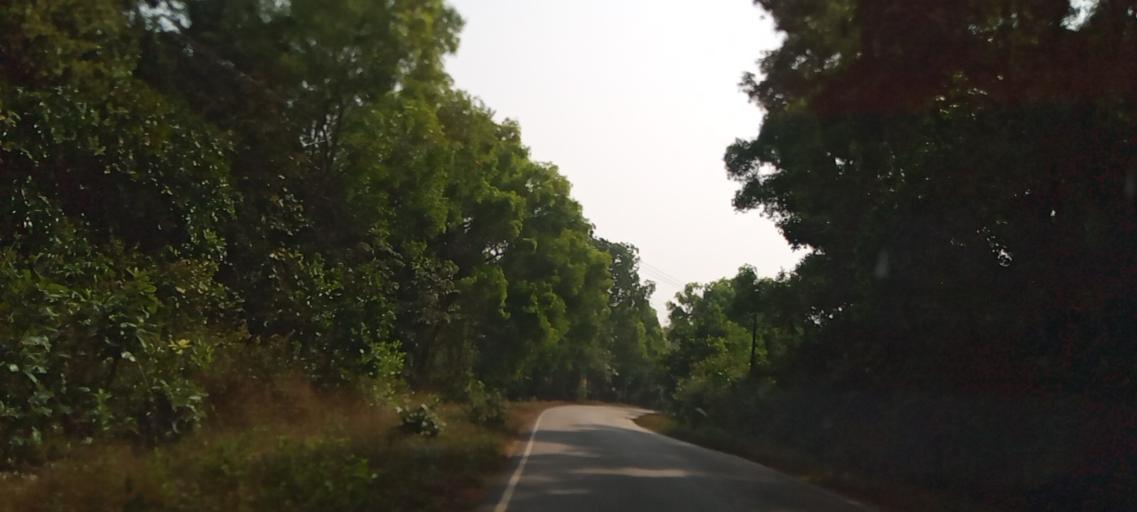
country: IN
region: Karnataka
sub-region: Udupi
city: Manipala
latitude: 13.5131
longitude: 74.8080
